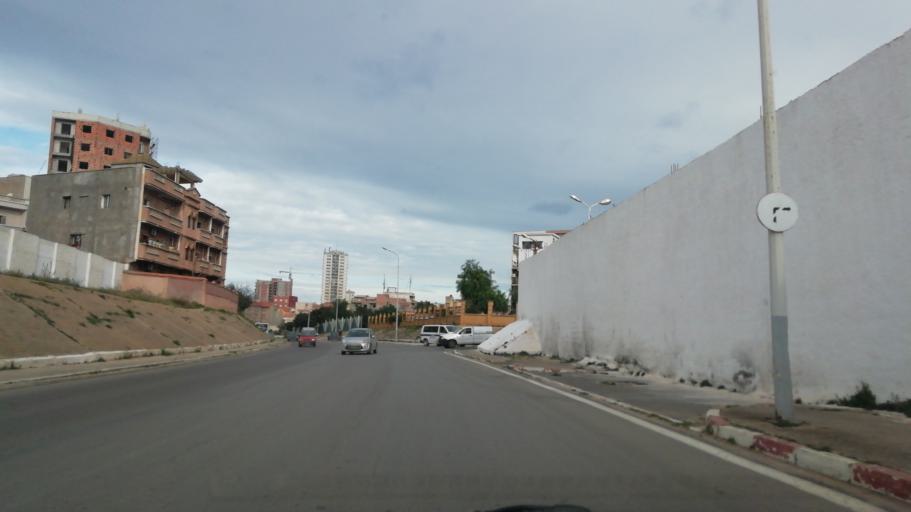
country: DZ
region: Oran
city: Oran
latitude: 35.7007
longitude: -0.6135
